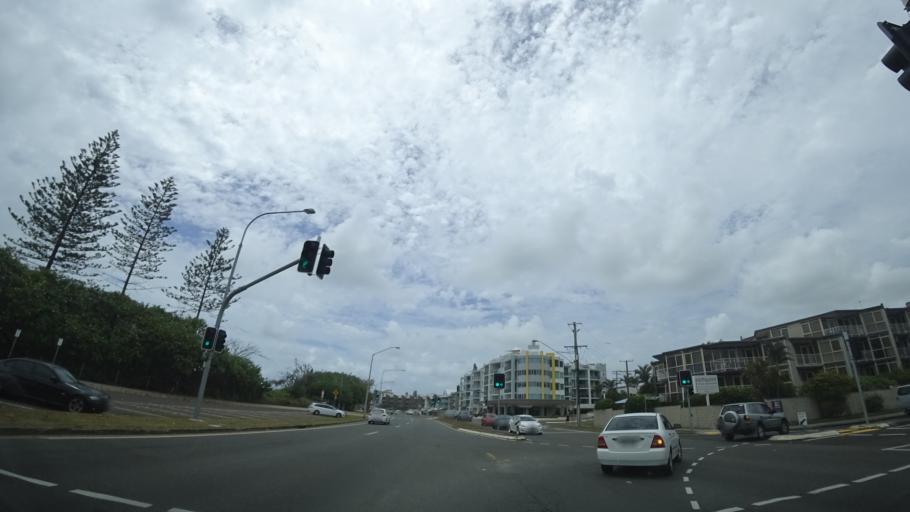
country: AU
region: Queensland
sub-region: Sunshine Coast
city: Mooloolaba
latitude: -26.6704
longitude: 153.1078
